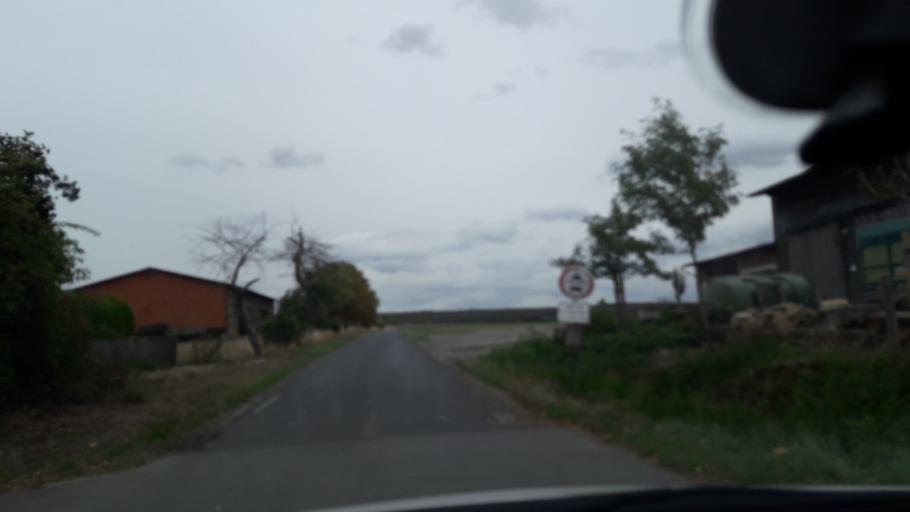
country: DE
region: Lower Saxony
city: Flothe
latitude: 52.0876
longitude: 10.4738
